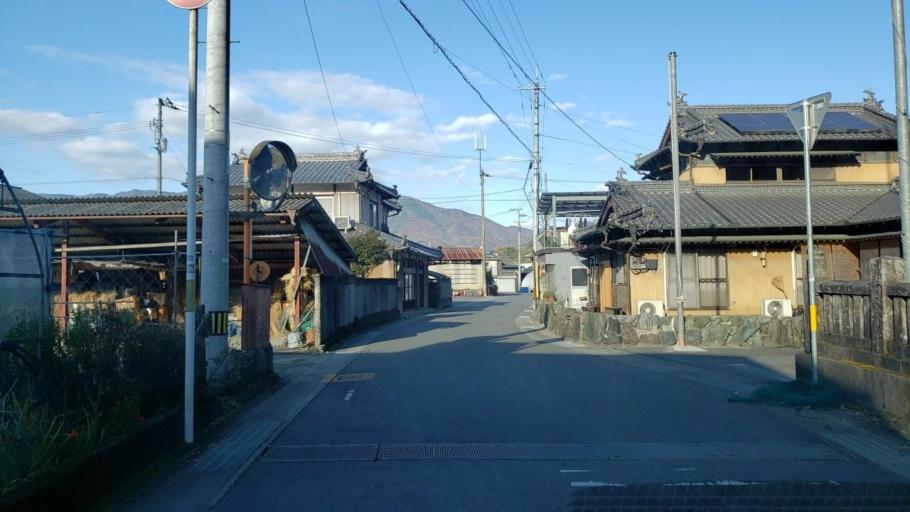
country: JP
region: Tokushima
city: Wakimachi
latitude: 34.0272
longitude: 134.0299
